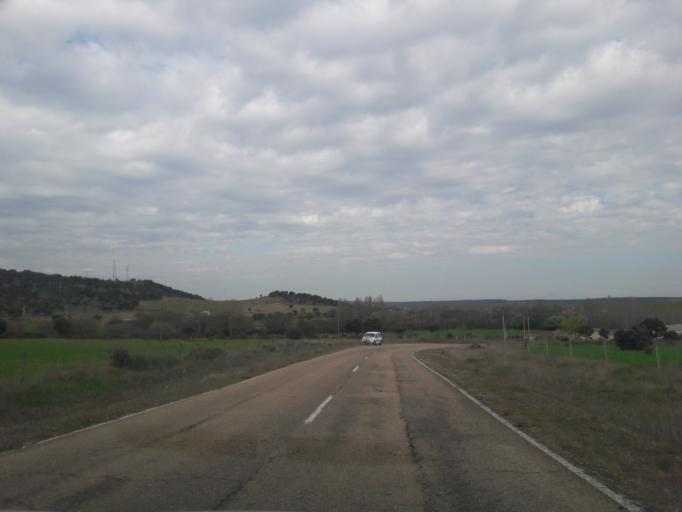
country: ES
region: Castille and Leon
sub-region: Provincia de Salamanca
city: Ciudad Rodrigo
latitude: 40.5775
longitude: -6.5356
